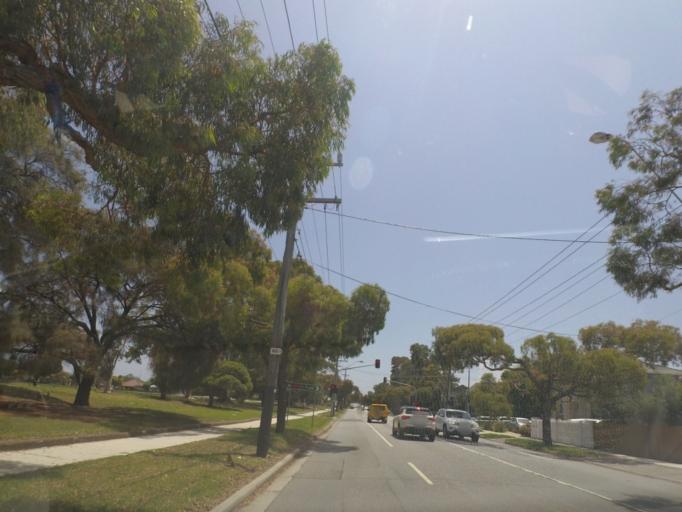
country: AU
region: Victoria
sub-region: Bayside
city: Hampton East
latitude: -37.9433
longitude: 145.0227
